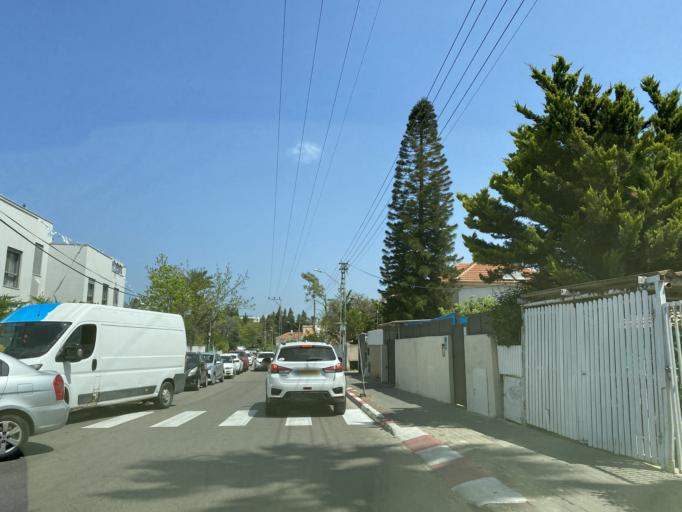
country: IL
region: Tel Aviv
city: Ramat HaSharon
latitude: 32.1542
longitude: 34.8364
